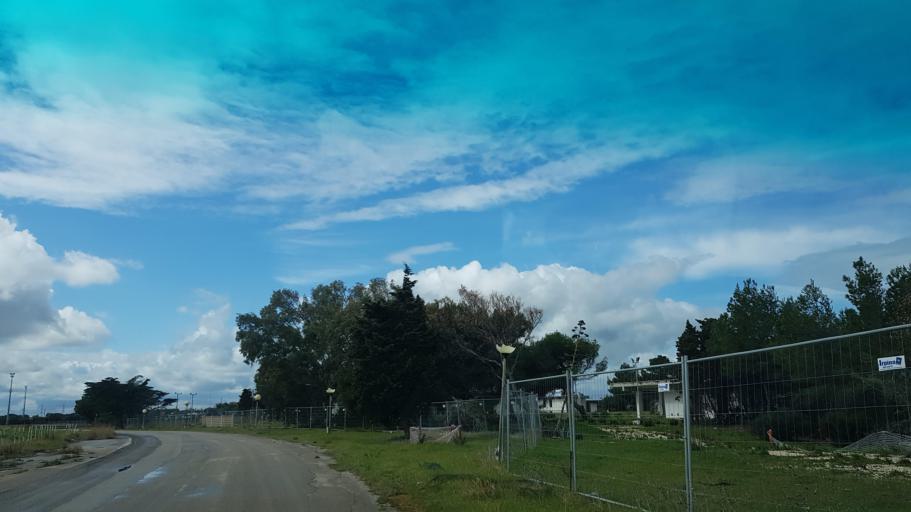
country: IT
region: Apulia
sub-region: Provincia di Brindisi
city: Materdomini
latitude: 40.6463
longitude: 17.9960
